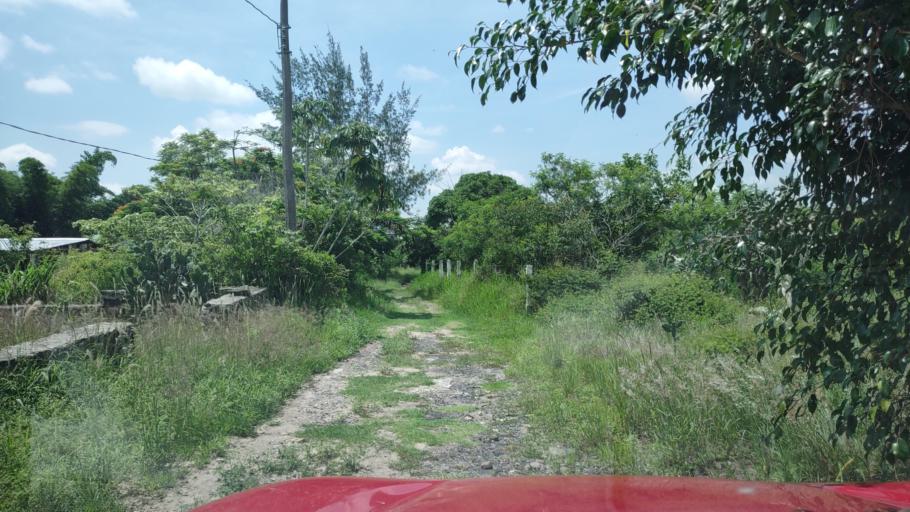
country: MX
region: Veracruz
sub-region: Emiliano Zapata
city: Dos Rios
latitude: 19.4615
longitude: -96.7886
